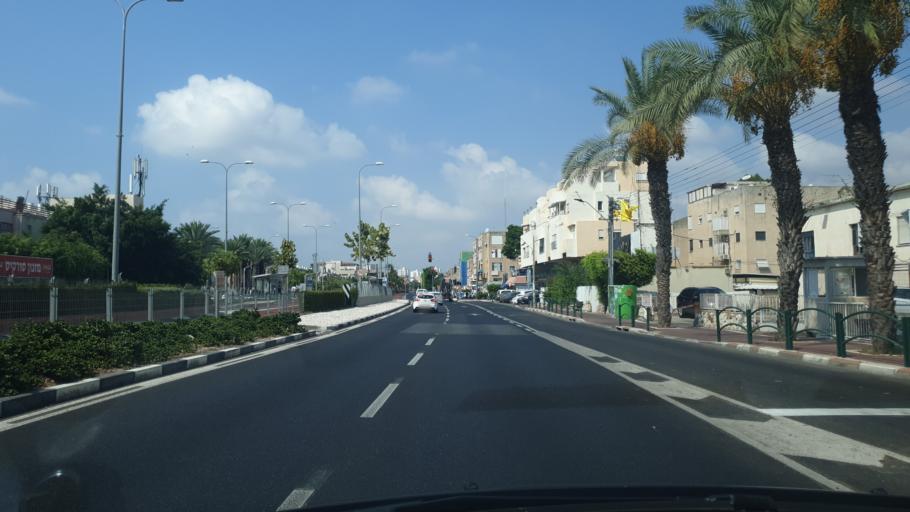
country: IL
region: Haifa
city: Qiryat Bialik
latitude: 32.8229
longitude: 35.0796
